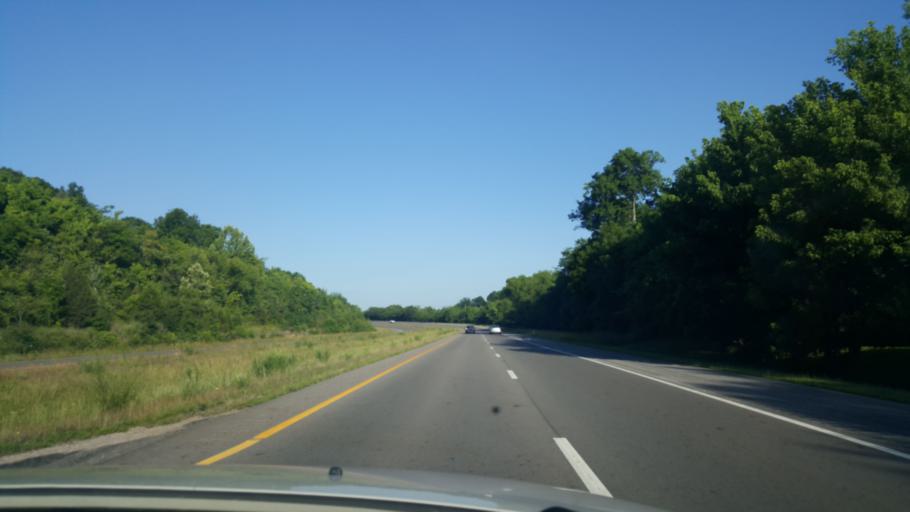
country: US
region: Tennessee
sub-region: Maury County
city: Columbia
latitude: 35.6299
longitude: -87.0963
